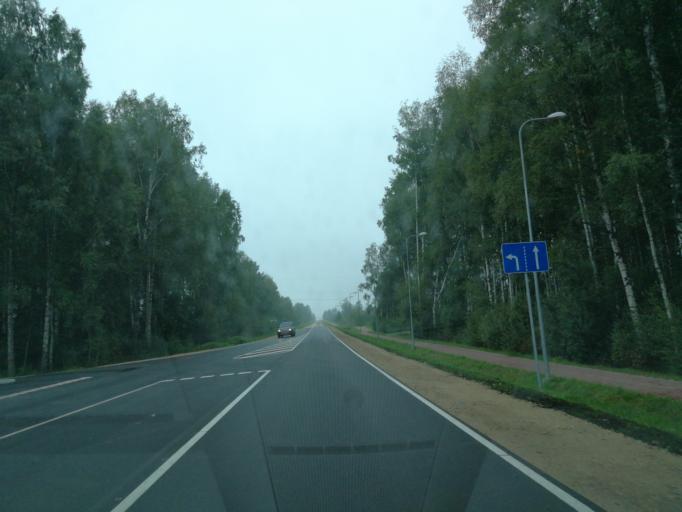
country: LV
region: Preilu Rajons
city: Preili
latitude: 56.2987
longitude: 26.7036
